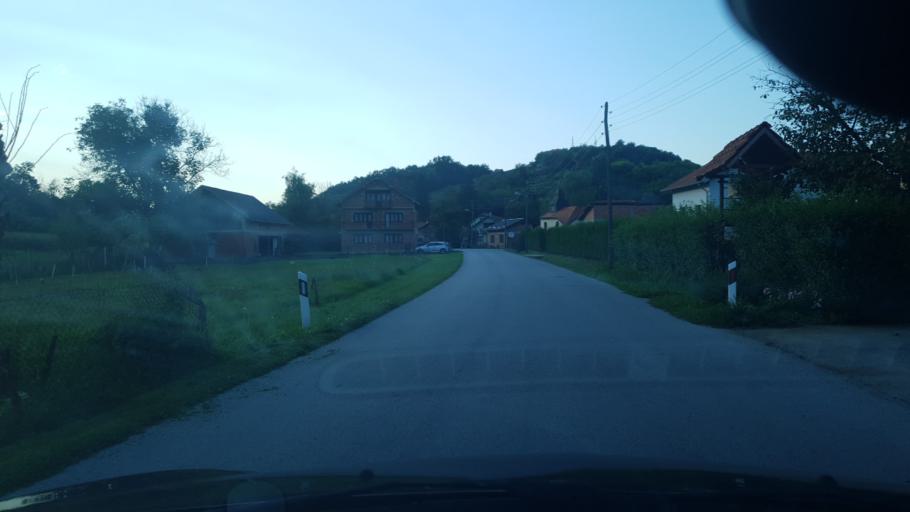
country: HR
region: Krapinsko-Zagorska
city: Zabok
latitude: 46.0333
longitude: 15.8982
